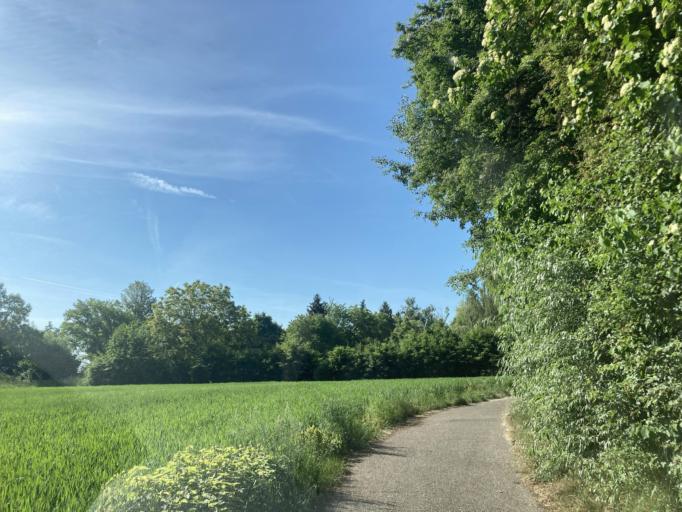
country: DE
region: Baden-Wuerttemberg
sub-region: Karlsruhe Region
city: Kronau
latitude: 49.2072
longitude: 8.6361
